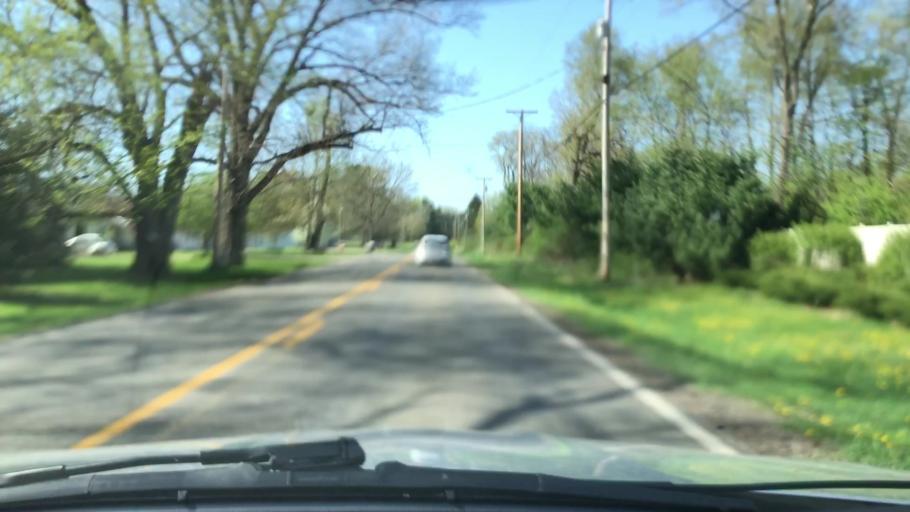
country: US
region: Indiana
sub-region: Saint Joseph County
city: Georgetown
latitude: 41.7535
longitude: -86.3019
